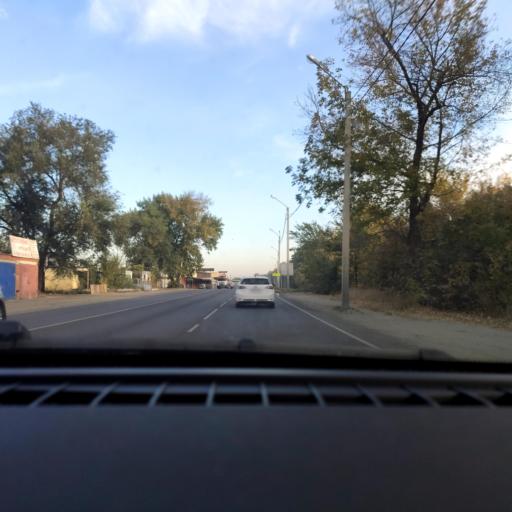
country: RU
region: Voronezj
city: Voronezh
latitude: 51.6704
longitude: 39.2717
